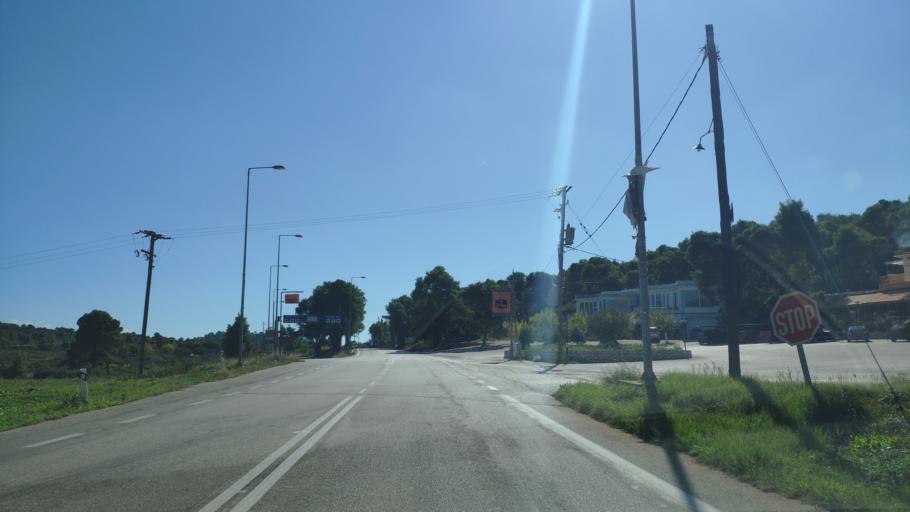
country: GR
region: Peloponnese
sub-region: Nomos Korinthias
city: Sofikon
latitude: 37.7867
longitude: 23.0759
